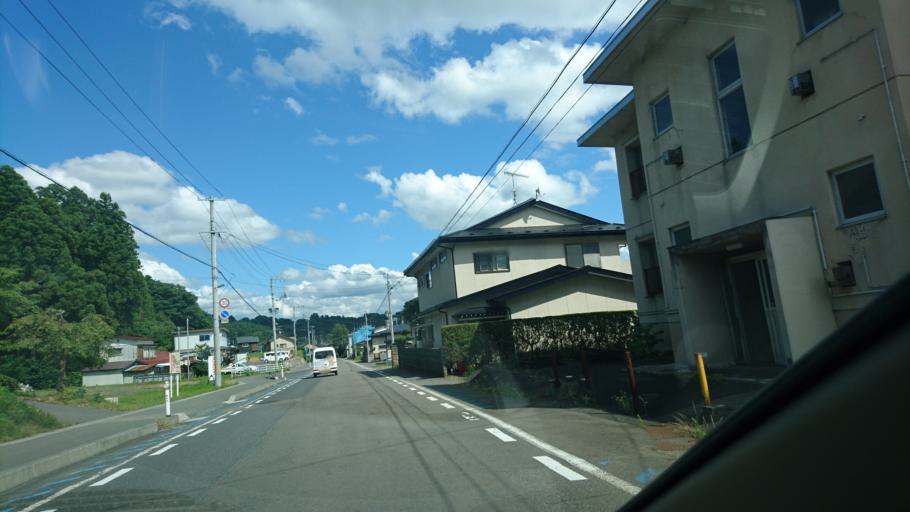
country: JP
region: Iwate
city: Mizusawa
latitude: 39.2006
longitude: 141.1677
